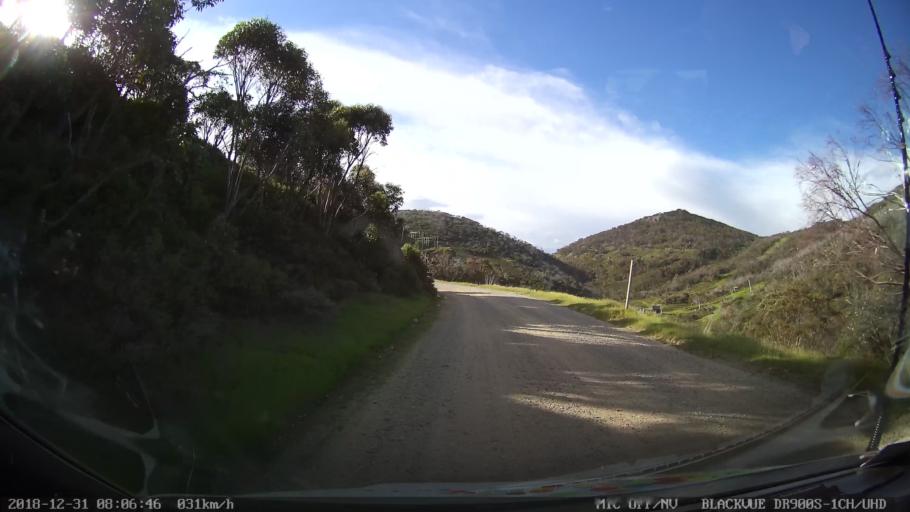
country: AU
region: New South Wales
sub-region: Snowy River
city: Jindabyne
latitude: -36.3758
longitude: 148.4084
